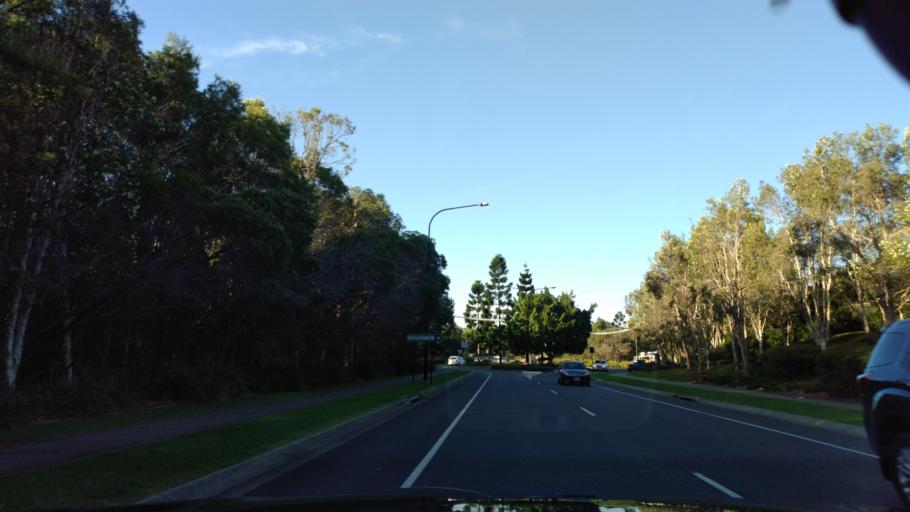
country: AU
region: Queensland
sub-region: Moreton Bay
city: Mango Hill
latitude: -27.2238
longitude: 153.0218
